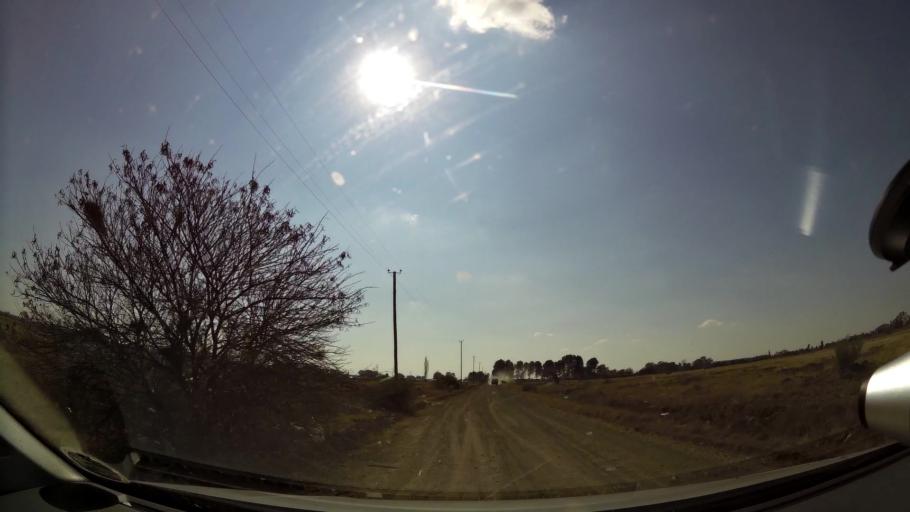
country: ZA
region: Orange Free State
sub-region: Mangaung Metropolitan Municipality
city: Bloemfontein
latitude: -29.1762
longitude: 26.3061
